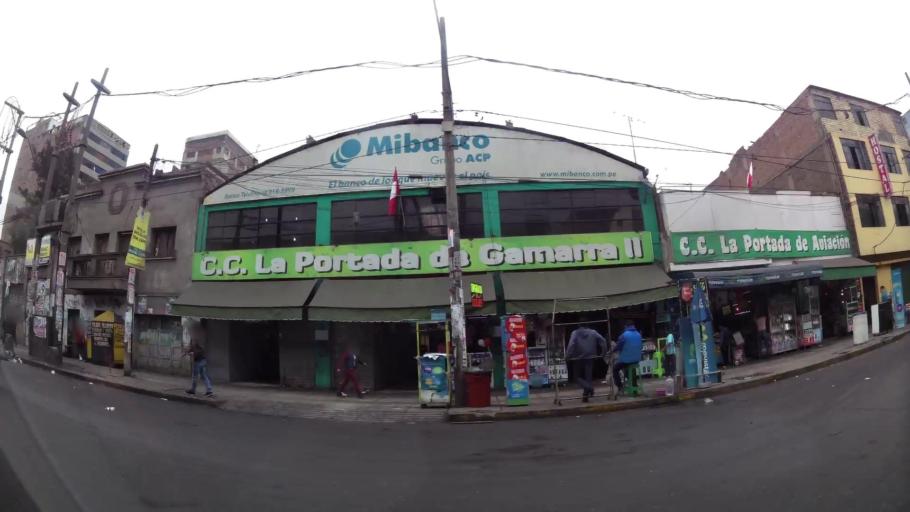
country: PE
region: Lima
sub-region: Lima
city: San Luis
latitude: -12.0686
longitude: -77.0121
